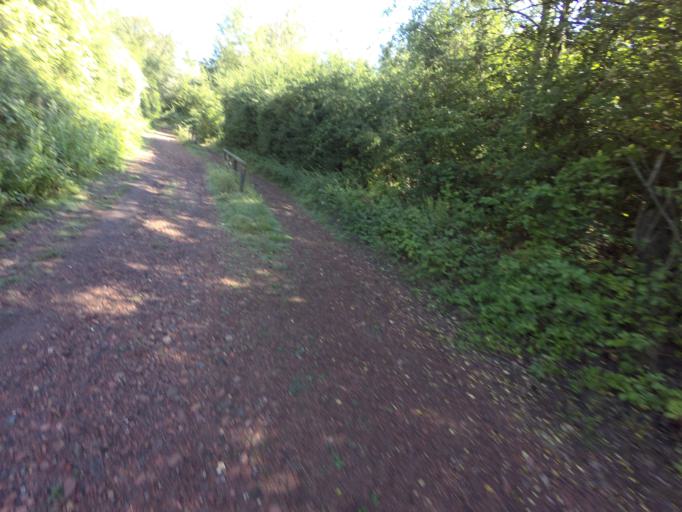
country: DE
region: North Rhine-Westphalia
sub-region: Regierungsbezirk Koln
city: Wurselen
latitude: 50.8276
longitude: 6.1116
